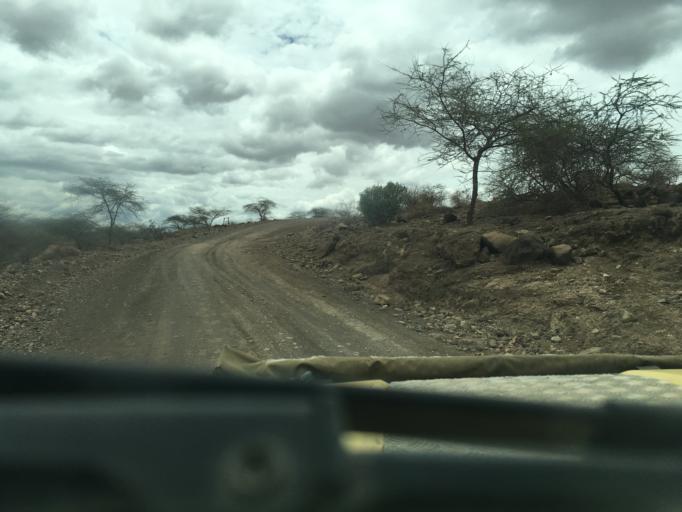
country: TZ
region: Arusha
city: Mto wa Mbu
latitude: -3.0950
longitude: 36.0185
